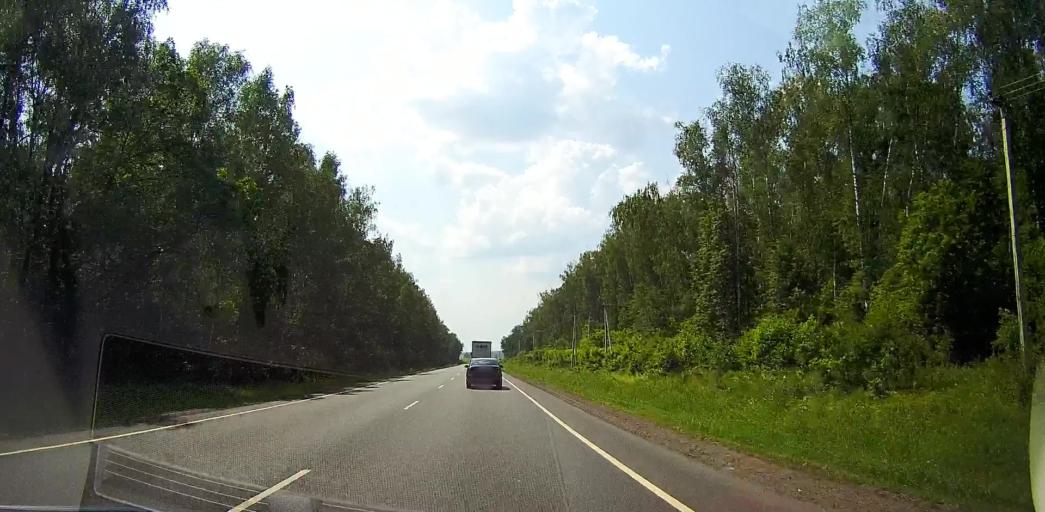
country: RU
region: Moskovskaya
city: Malino
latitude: 55.1387
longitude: 38.2723
